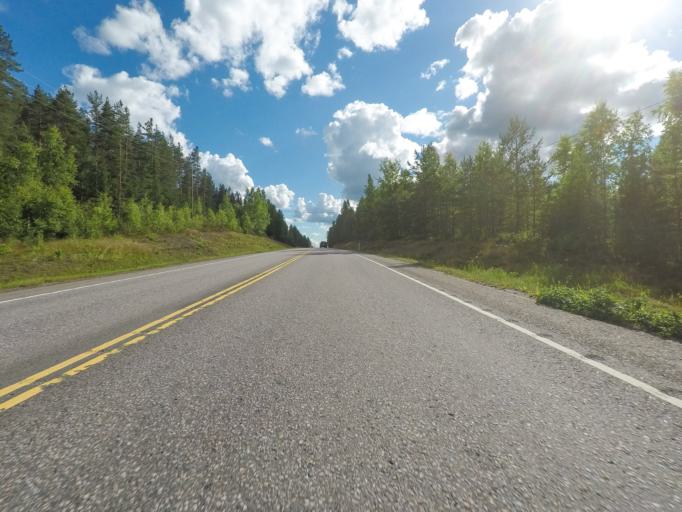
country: FI
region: Uusimaa
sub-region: Helsinki
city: Nurmijaervi
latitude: 60.5182
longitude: 24.6505
